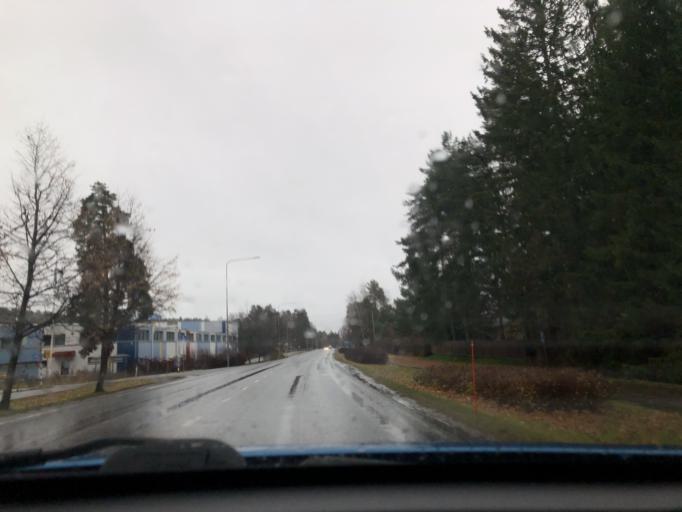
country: FI
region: Pirkanmaa
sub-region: Tampere
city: Kangasala
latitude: 61.4711
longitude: 24.0324
